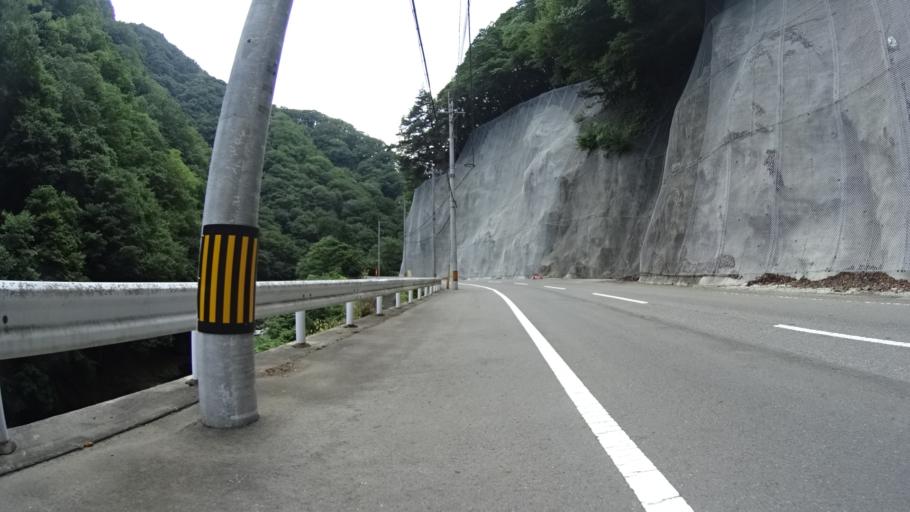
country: JP
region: Gunma
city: Tomioka
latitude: 36.0790
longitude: 138.7096
